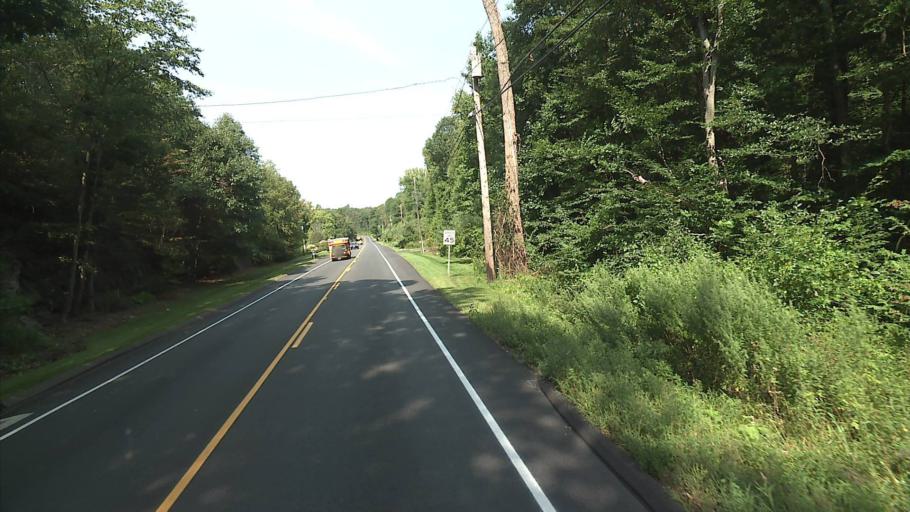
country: US
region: Connecticut
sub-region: Fairfield County
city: Bethel
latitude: 41.3544
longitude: -73.3810
